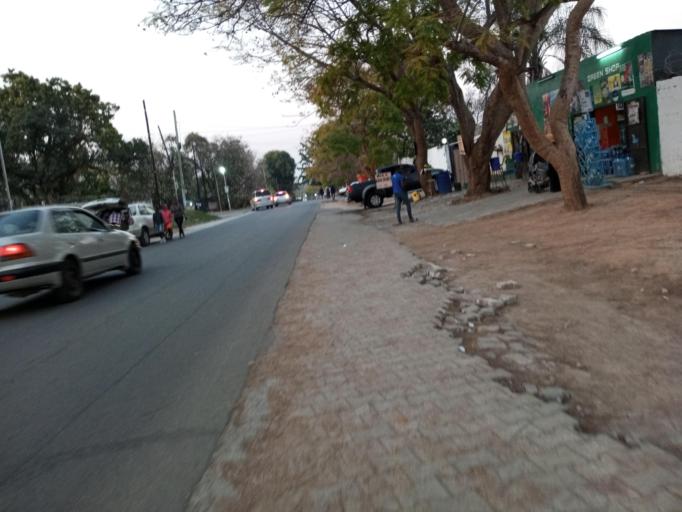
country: ZM
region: Lusaka
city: Lusaka
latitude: -15.4020
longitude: 28.2966
